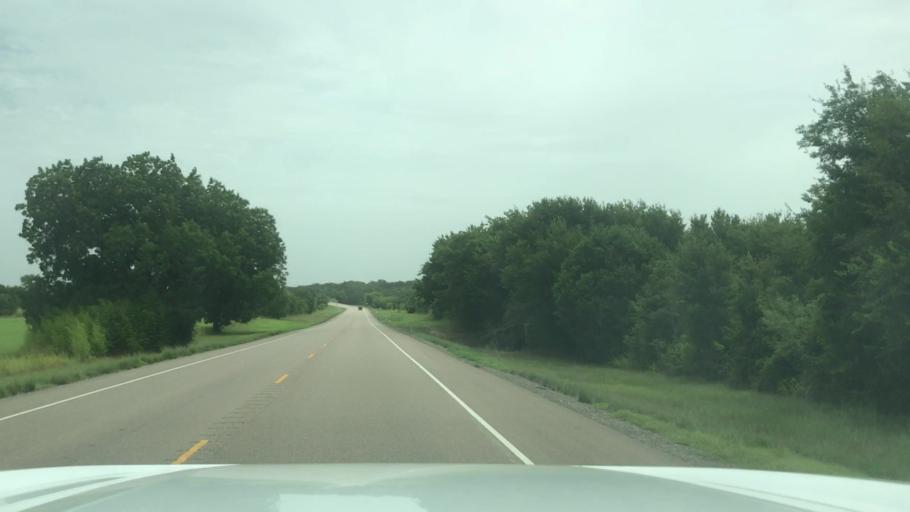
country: US
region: Texas
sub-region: Hamilton County
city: Hico
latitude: 31.9774
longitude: -97.8879
